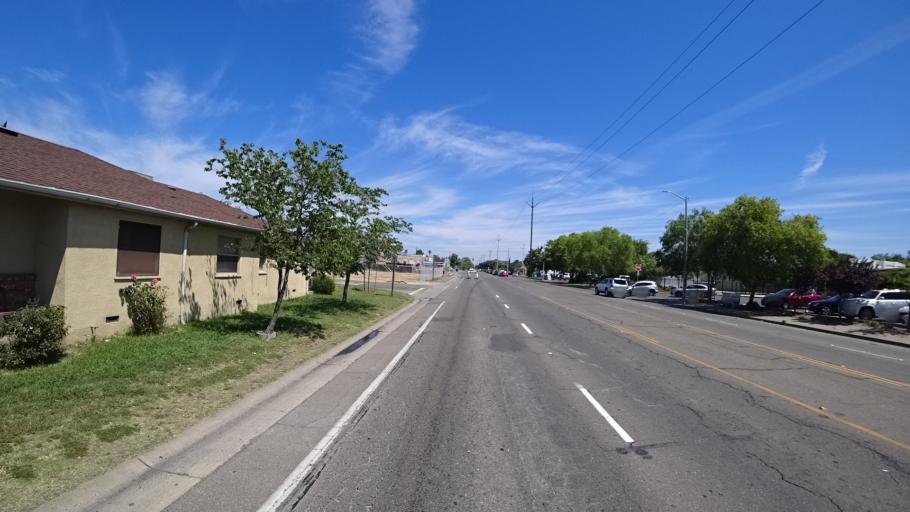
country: US
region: California
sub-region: Sacramento County
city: Arden-Arcade
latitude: 38.6089
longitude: -121.4154
